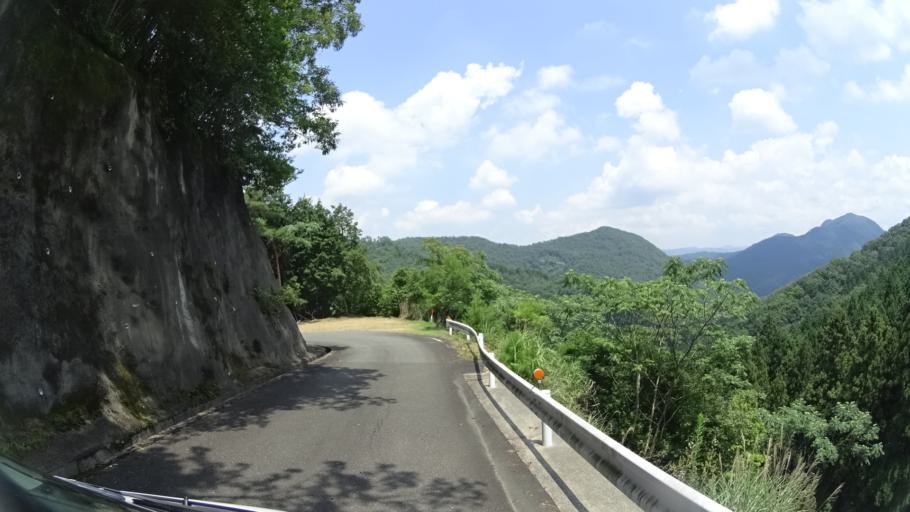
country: JP
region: Hyogo
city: Sasayama
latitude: 35.1703
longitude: 135.2023
